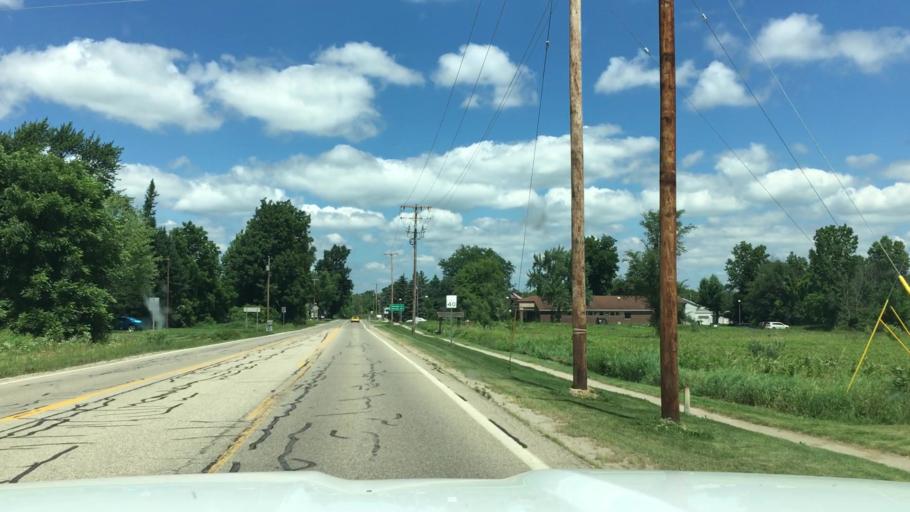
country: US
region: Michigan
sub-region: Barry County
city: Stony Point
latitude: 42.5039
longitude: -85.4086
